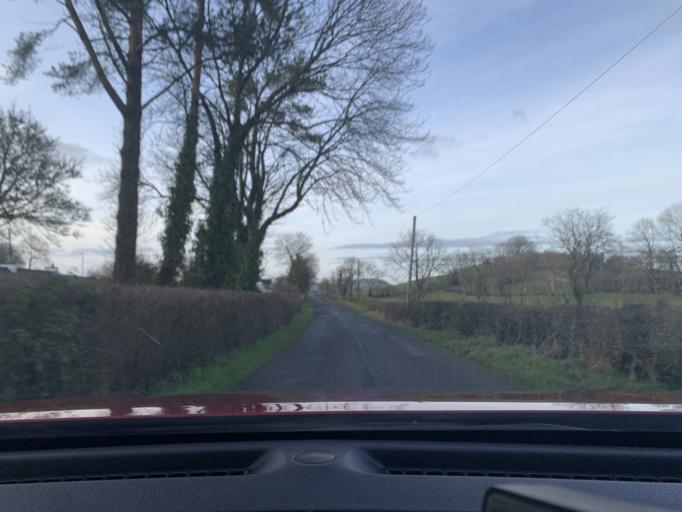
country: IE
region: Connaught
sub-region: Sligo
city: Ballymote
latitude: 54.1331
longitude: -8.5847
